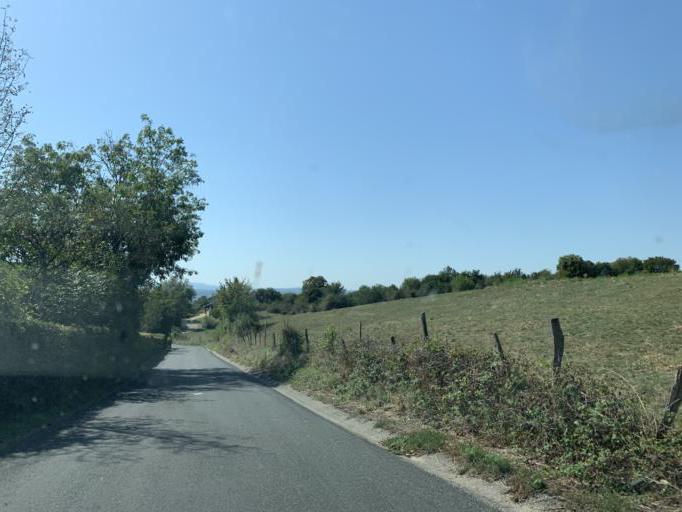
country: FR
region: Rhone-Alpes
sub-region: Departement de la Savoie
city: Saint-Genix-sur-Guiers
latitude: 45.6488
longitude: 5.6334
